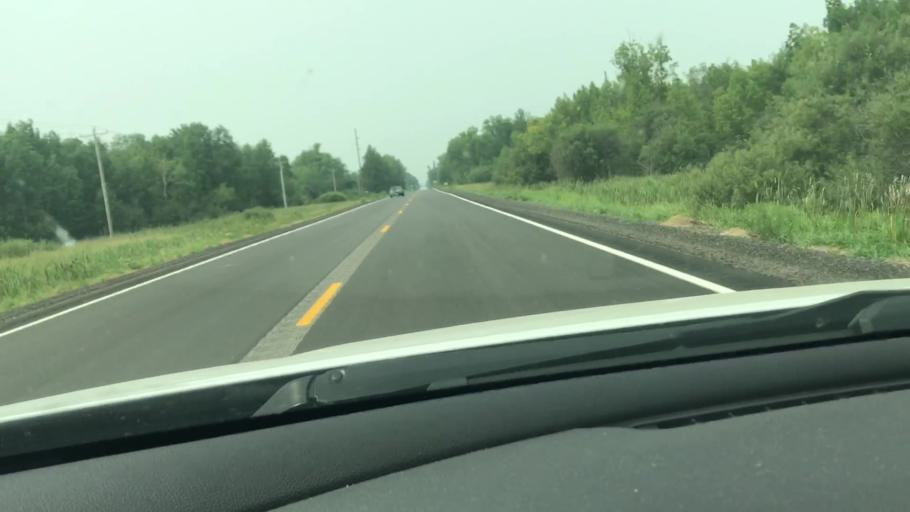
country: US
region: Minnesota
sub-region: Itasca County
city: Cohasset
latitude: 47.3640
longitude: -93.8714
